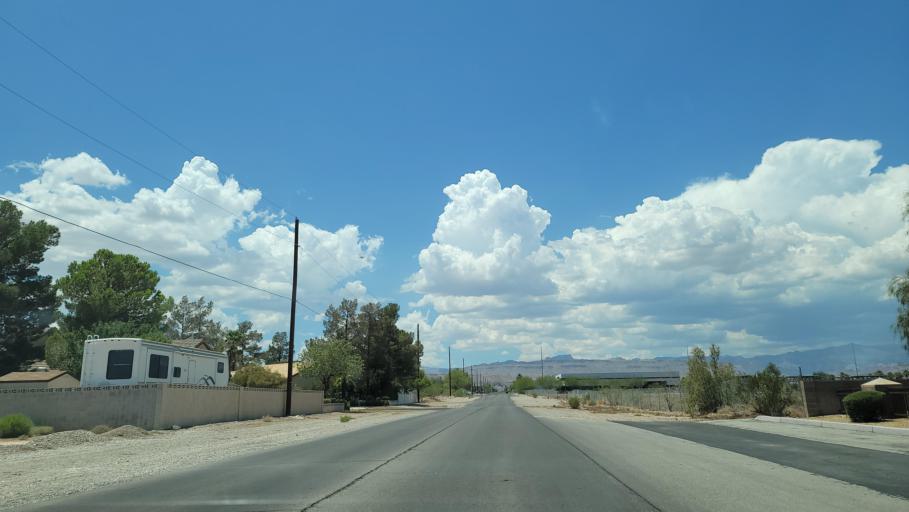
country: US
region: Nevada
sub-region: Clark County
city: Spring Valley
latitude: 36.0780
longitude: -115.2367
